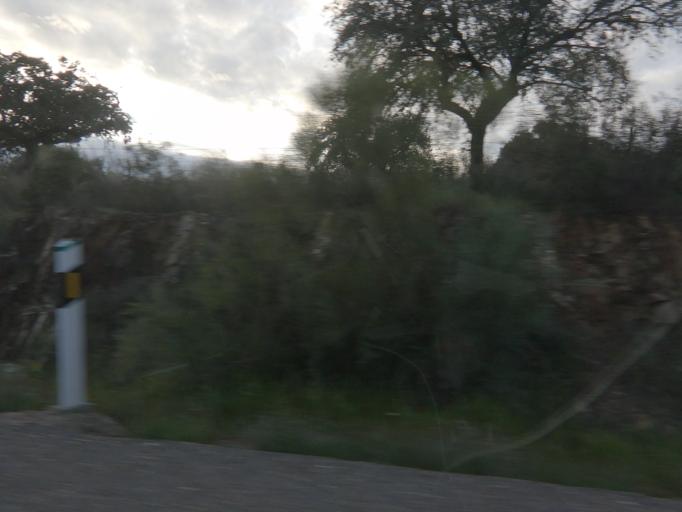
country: ES
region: Extremadura
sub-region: Provincia de Badajoz
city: Puebla de Obando
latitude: 39.1501
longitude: -6.6499
